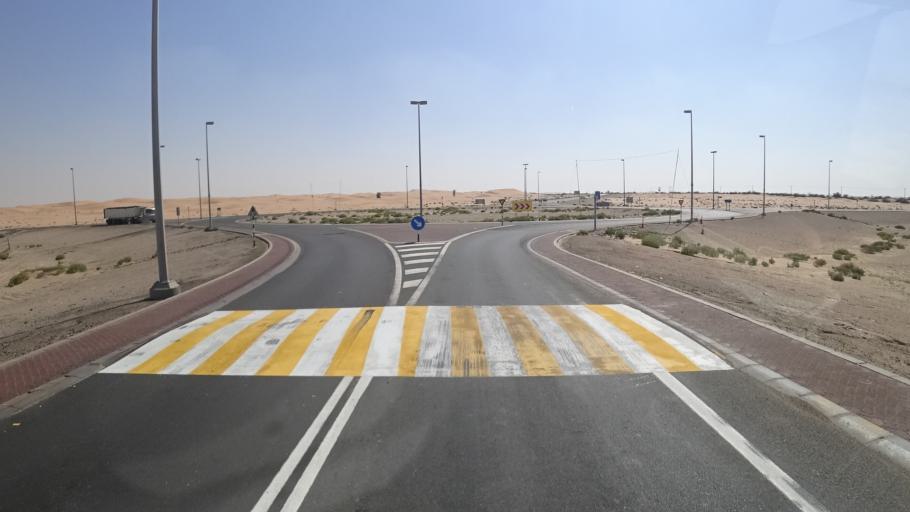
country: AE
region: Abu Dhabi
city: Al Ain
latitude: 23.9928
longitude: 55.0965
